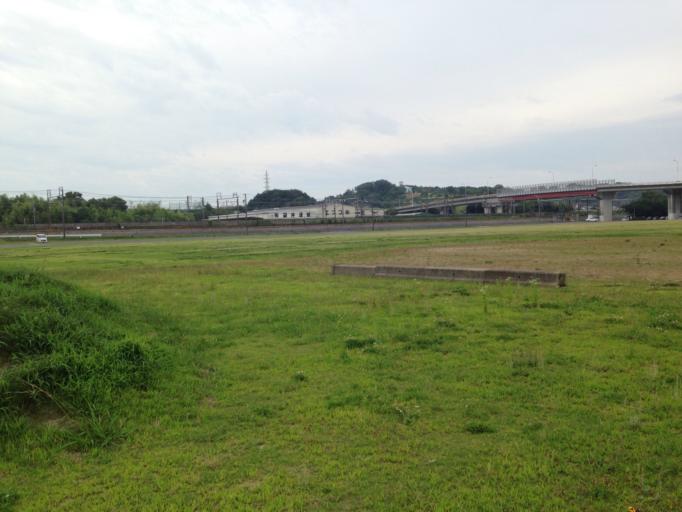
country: JP
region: Shizuoka
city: Fukuroi
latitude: 34.7486
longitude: 137.9447
